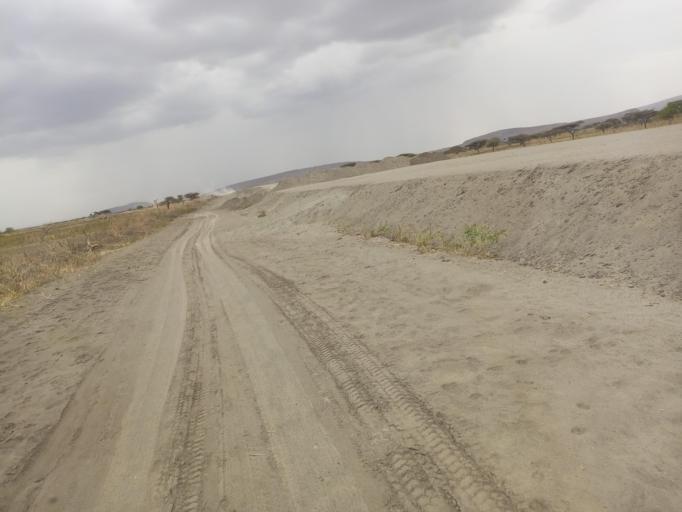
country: ET
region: Oromiya
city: Ziway
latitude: 7.8475
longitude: 38.6618
